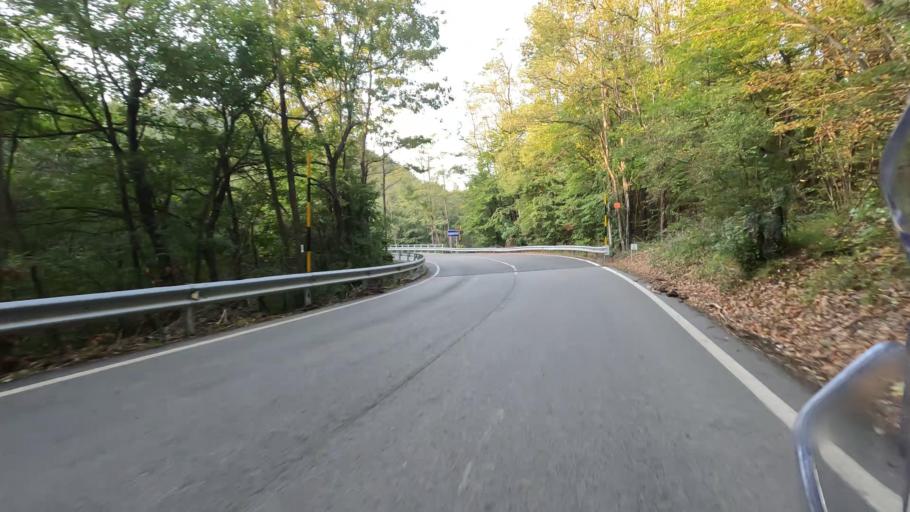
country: IT
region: Liguria
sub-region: Provincia di Savona
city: Sassello
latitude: 44.5059
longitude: 8.4828
